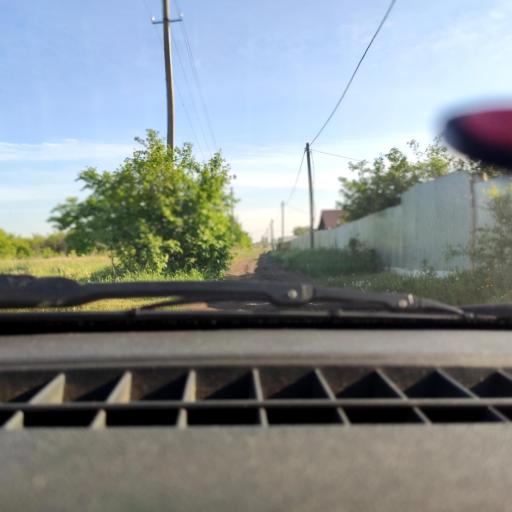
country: RU
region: Bashkortostan
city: Avdon
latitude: 54.4631
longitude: 55.8195
